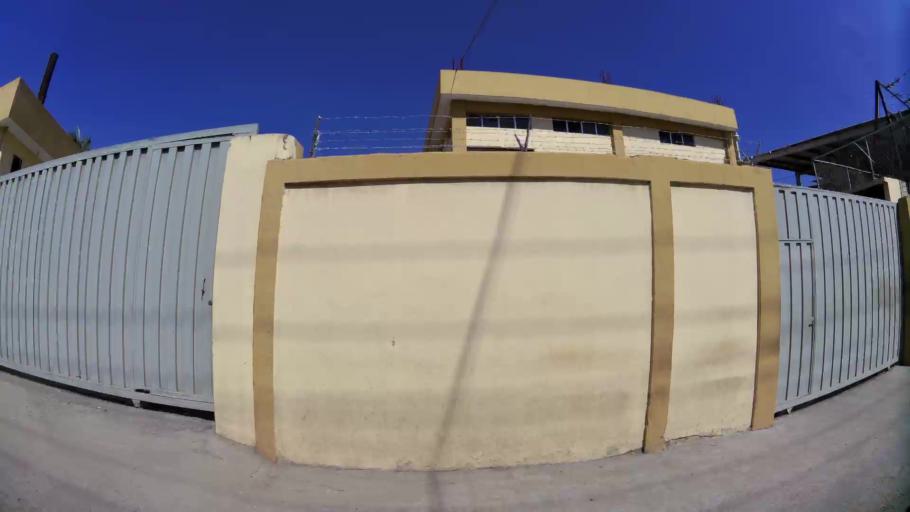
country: DO
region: Santo Domingo
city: Santo Domingo Oeste
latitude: 18.4778
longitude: -70.0011
